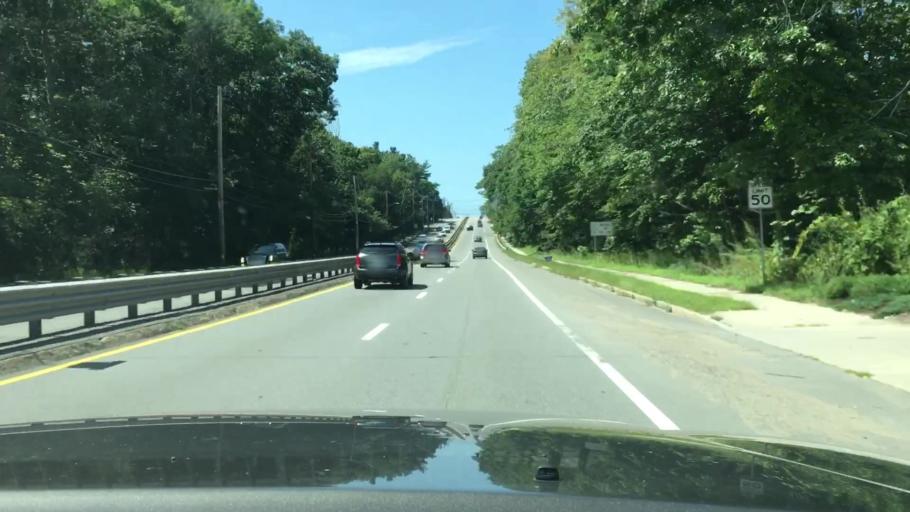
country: US
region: Massachusetts
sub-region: Middlesex County
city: Natick
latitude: 42.3020
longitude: -71.3419
